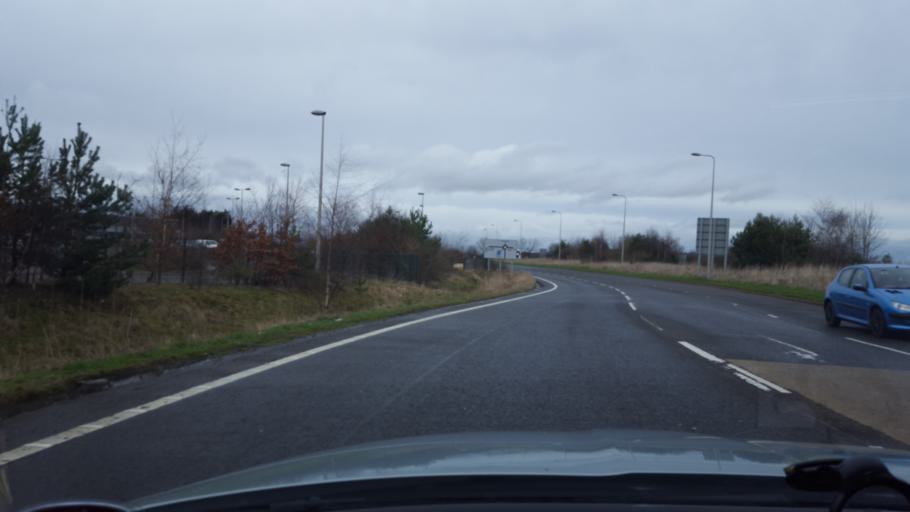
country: GB
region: Scotland
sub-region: Edinburgh
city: Currie
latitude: 55.9158
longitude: -3.3137
